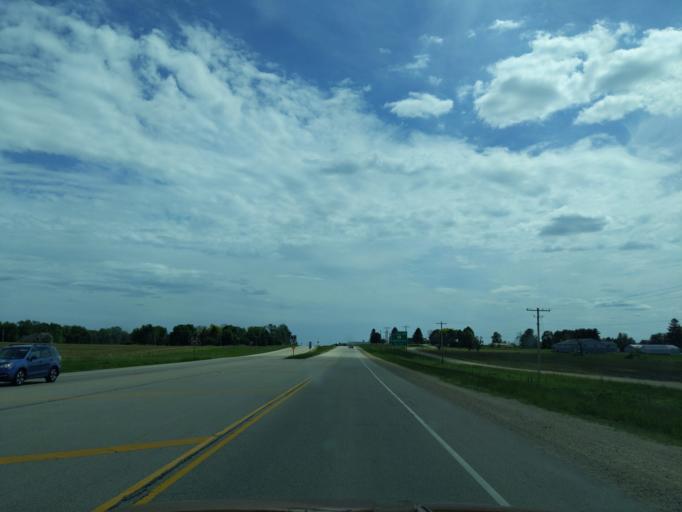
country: US
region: Wisconsin
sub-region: Dane County
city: De Forest
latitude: 43.2708
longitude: -89.3247
